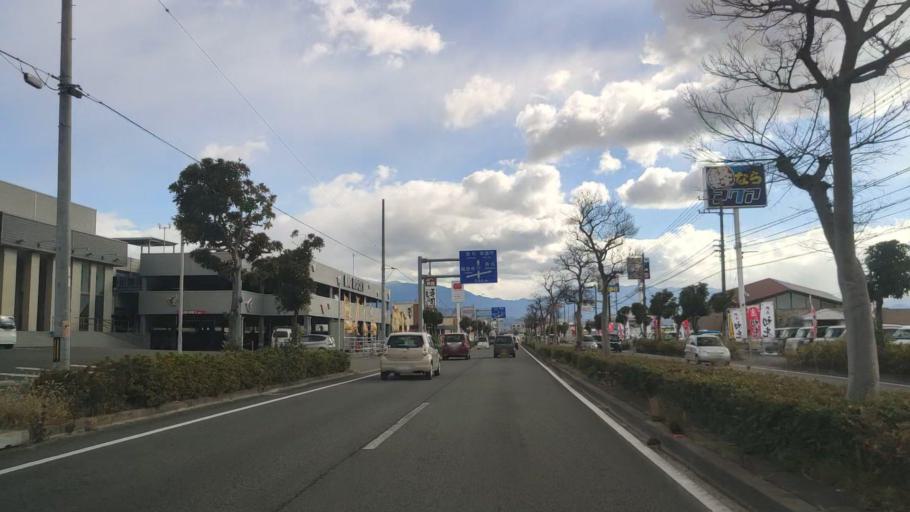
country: JP
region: Ehime
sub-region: Shikoku-chuo Shi
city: Matsuyama
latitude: 33.8171
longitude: 132.7939
